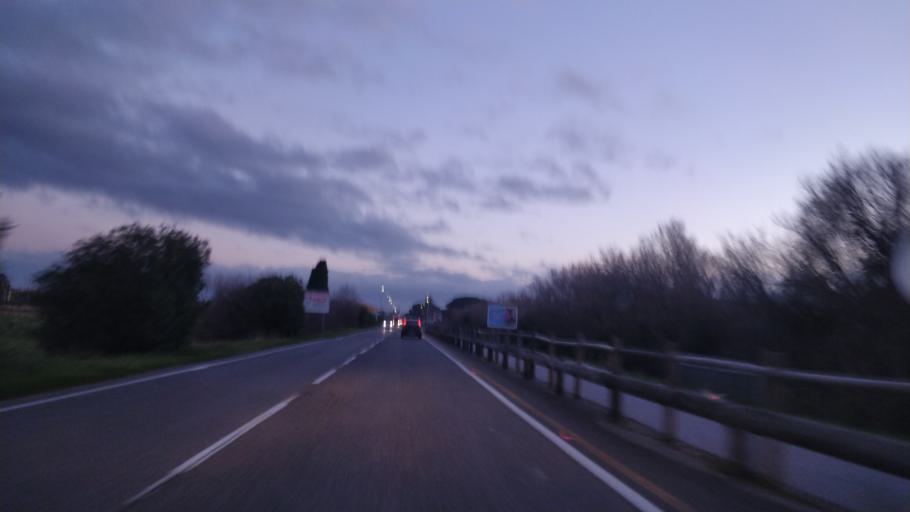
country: IT
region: Tuscany
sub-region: Provincia di Livorno
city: Vada
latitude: 43.3607
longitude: 10.4534
